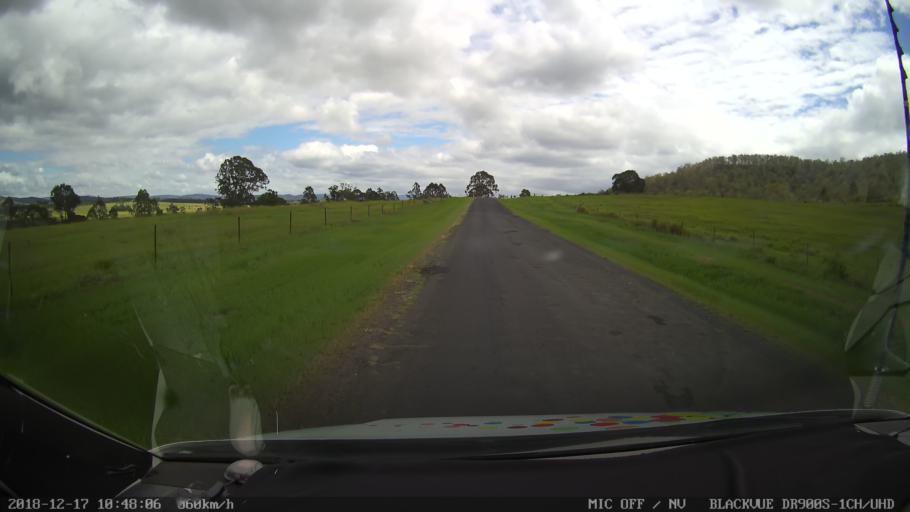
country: AU
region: New South Wales
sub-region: Clarence Valley
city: Gordon
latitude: -28.8756
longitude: 152.5706
